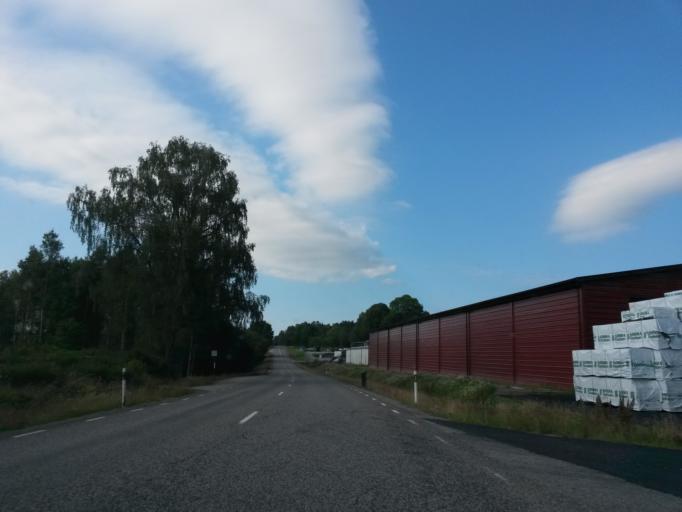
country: SE
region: Vaestra Goetaland
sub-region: Vargarda Kommun
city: Jonstorp
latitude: 58.0498
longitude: 12.6556
